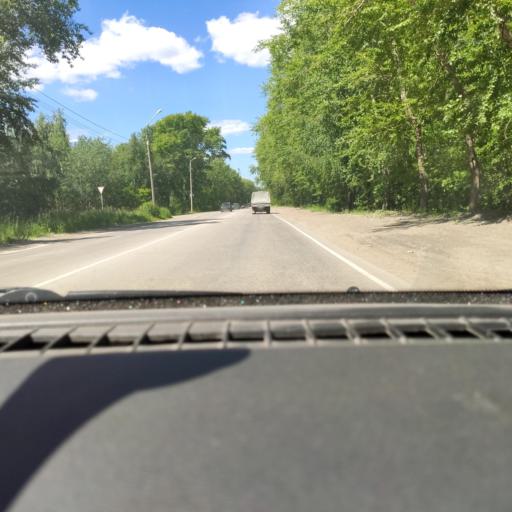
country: RU
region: Perm
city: Krasnokamsk
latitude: 58.0652
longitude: 55.7981
